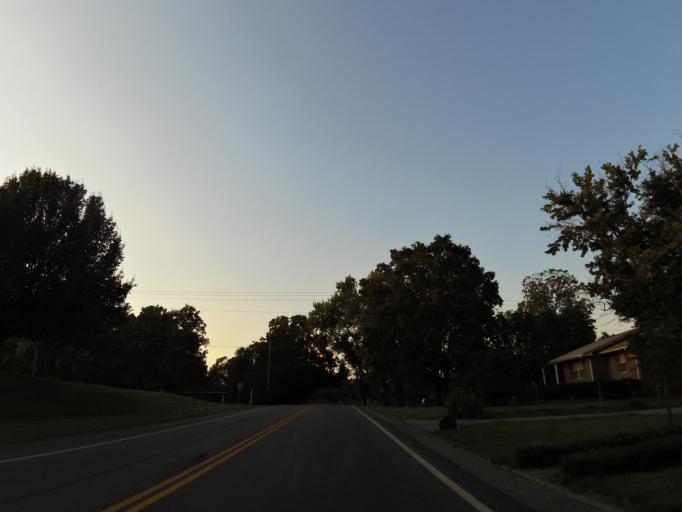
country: US
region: Tennessee
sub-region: Monroe County
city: Sweetwater
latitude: 35.6111
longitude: -84.4621
